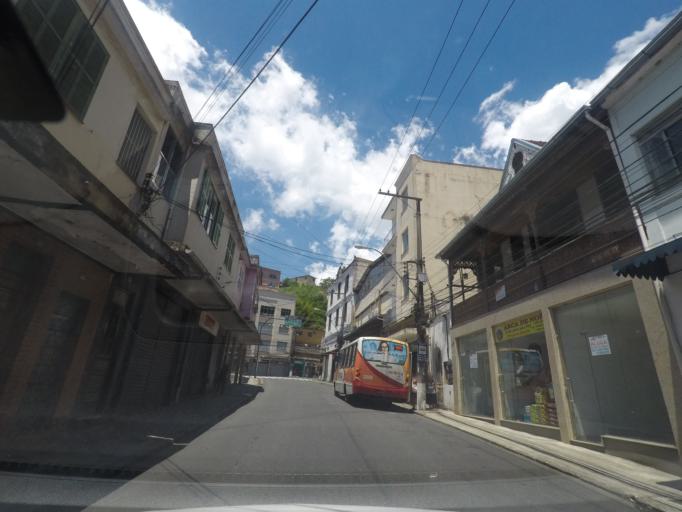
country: BR
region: Rio de Janeiro
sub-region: Petropolis
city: Petropolis
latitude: -22.5143
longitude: -43.1749
